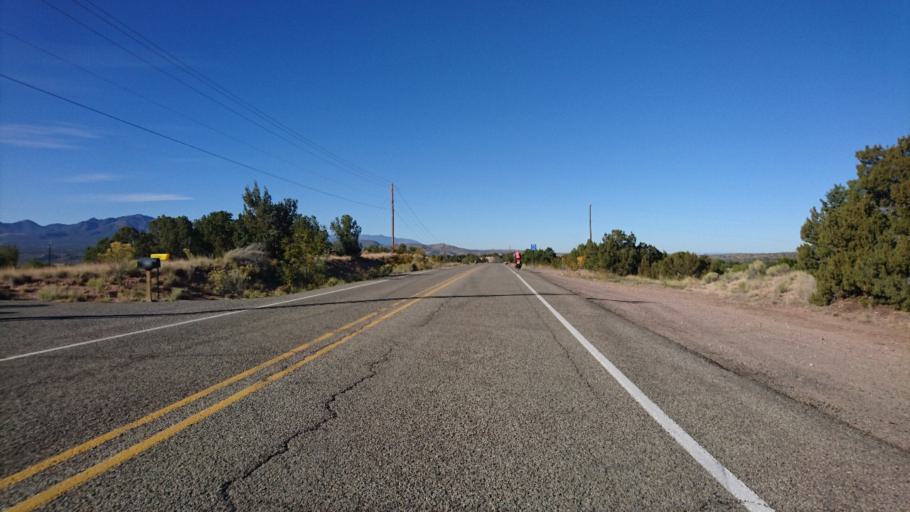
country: US
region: New Mexico
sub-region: Santa Fe County
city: La Cienega
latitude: 35.4522
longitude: -106.0734
